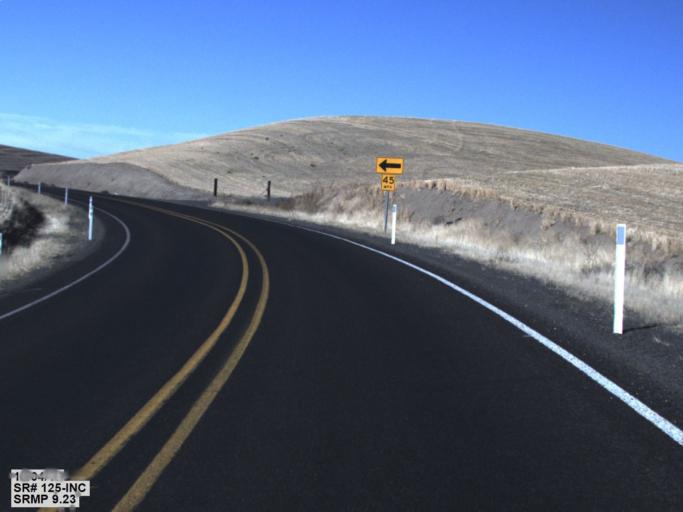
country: US
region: Washington
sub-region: Walla Walla County
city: Walla Walla
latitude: 46.1071
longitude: -118.3719
